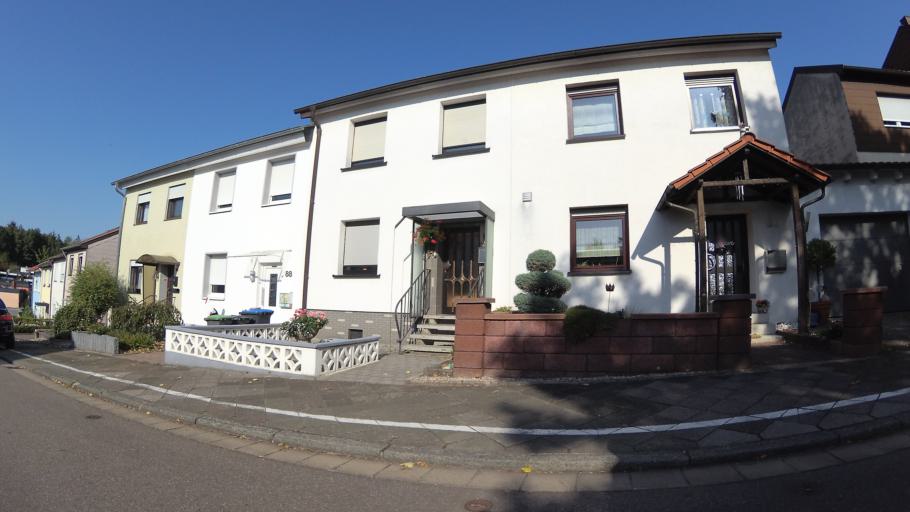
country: DE
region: Saarland
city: Sankt Ingbert
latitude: 49.2900
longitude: 7.1196
